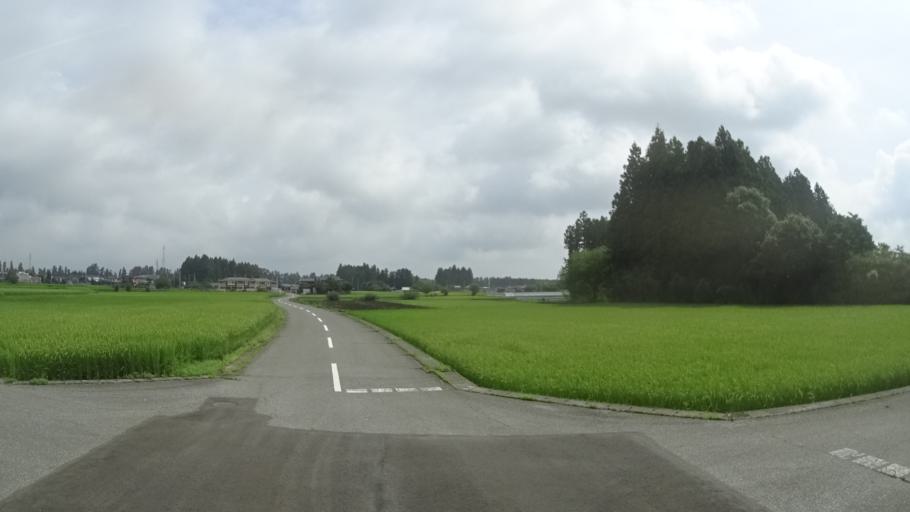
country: JP
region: Tochigi
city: Imaichi
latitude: 36.7114
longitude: 139.7004
